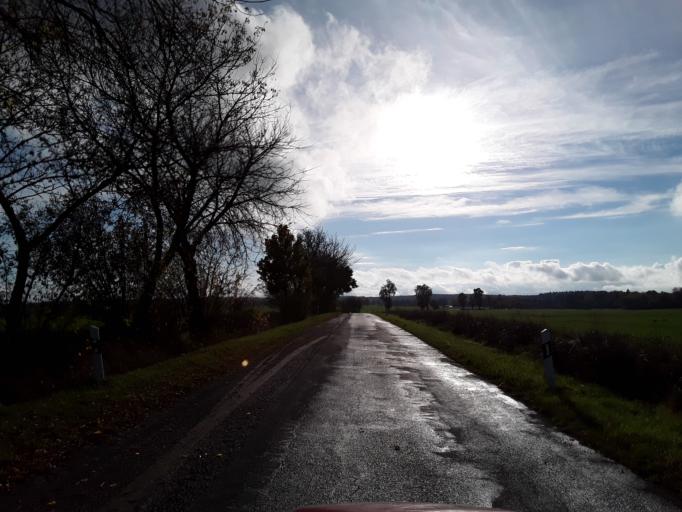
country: DE
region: Brandenburg
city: Mittenwalde
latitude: 53.2801
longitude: 13.7057
